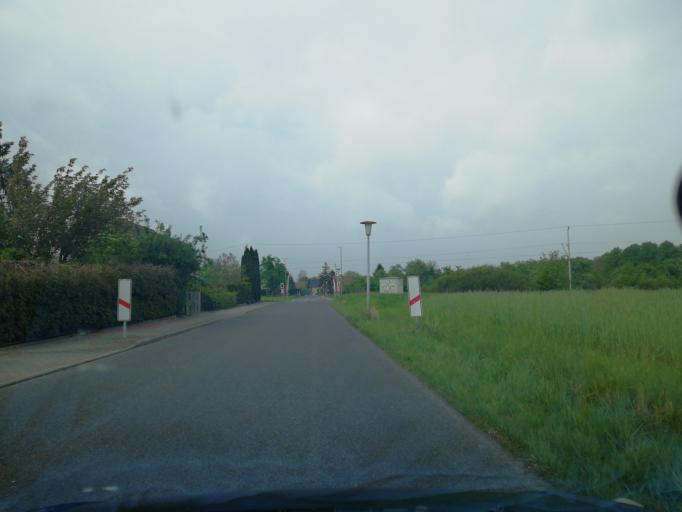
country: DE
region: Brandenburg
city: Calau
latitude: 51.7552
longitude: 13.9822
